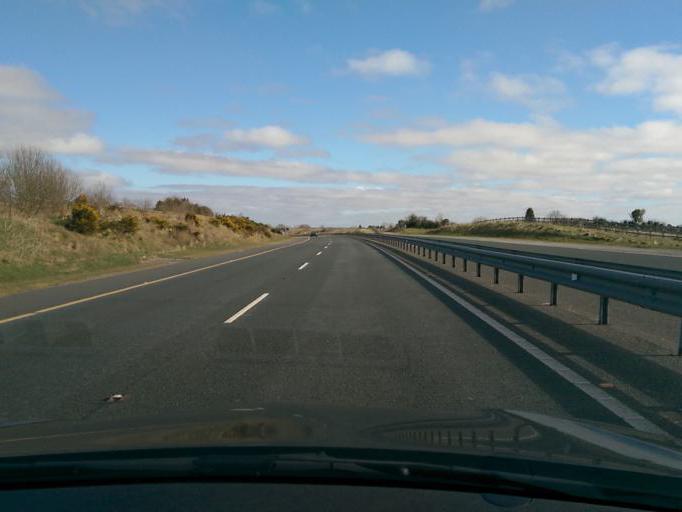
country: IE
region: Leinster
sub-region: An Iarmhi
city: Athlone
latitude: 53.3504
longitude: -8.0695
